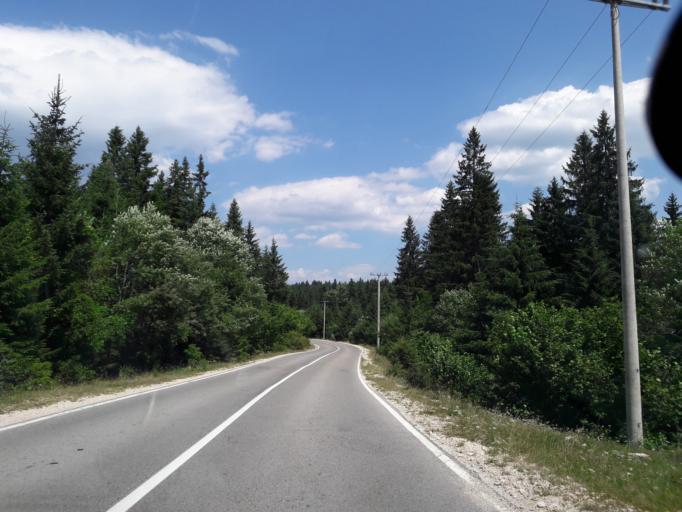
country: BA
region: Republika Srpska
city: Sipovo
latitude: 44.1224
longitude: 17.1797
